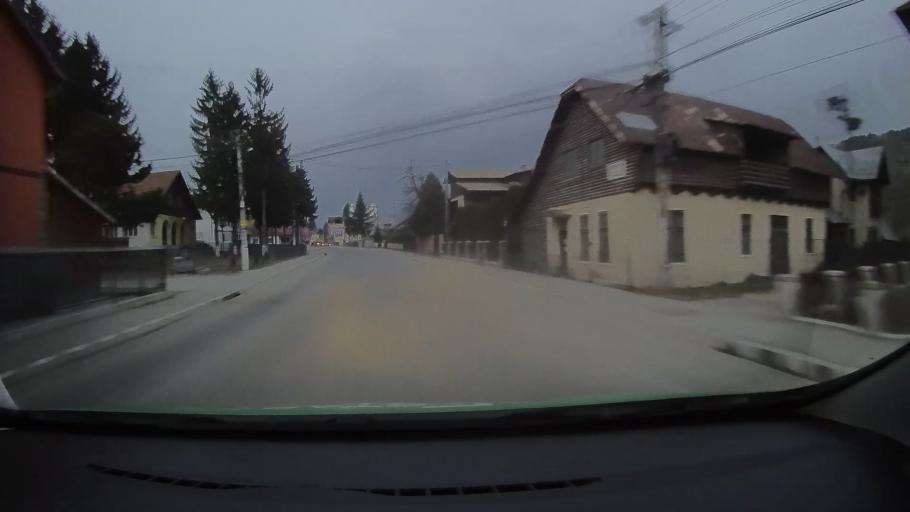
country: RO
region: Prahova
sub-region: Comuna Valea Doftanei
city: Tesila
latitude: 45.3003
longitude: 25.7213
